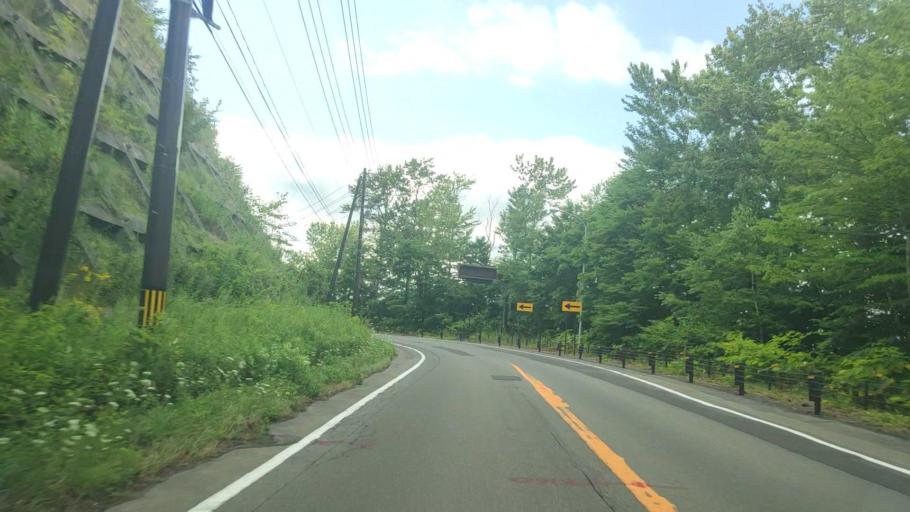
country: JP
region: Hokkaido
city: Date
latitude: 42.5639
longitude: 140.8836
